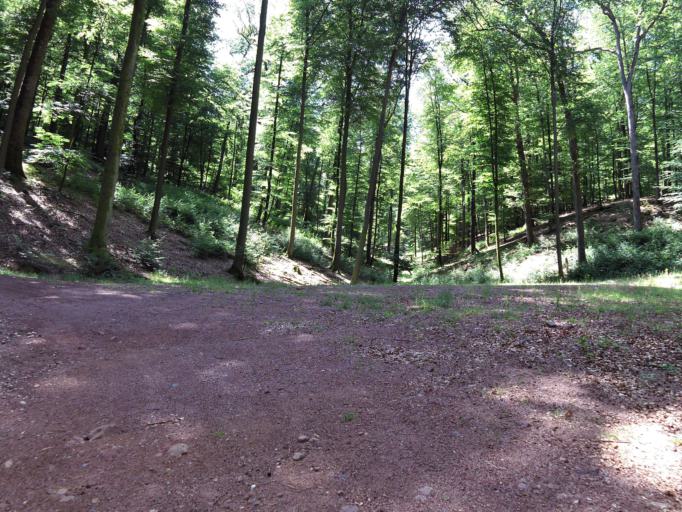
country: DE
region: Rheinland-Pfalz
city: Wilgartswiesen
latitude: 49.2691
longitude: 7.8599
